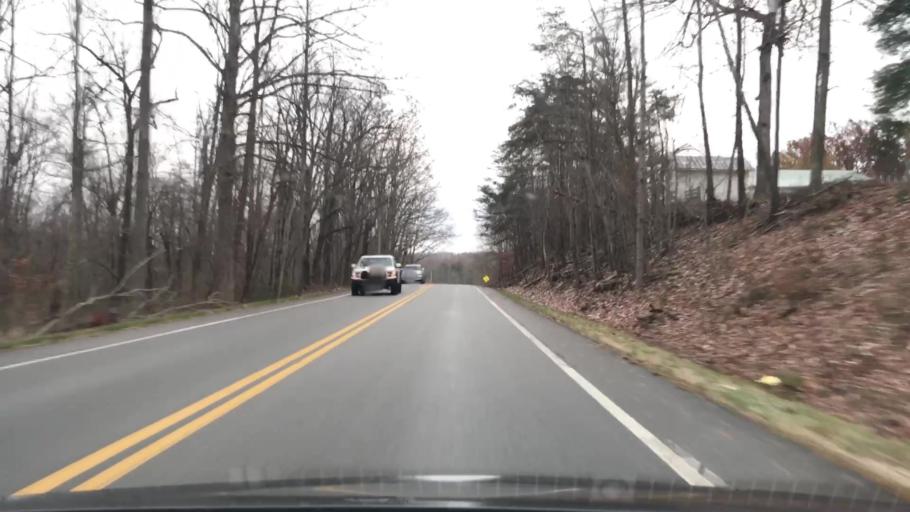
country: US
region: Tennessee
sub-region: Putnam County
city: Monterey
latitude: 36.1358
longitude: -85.2462
